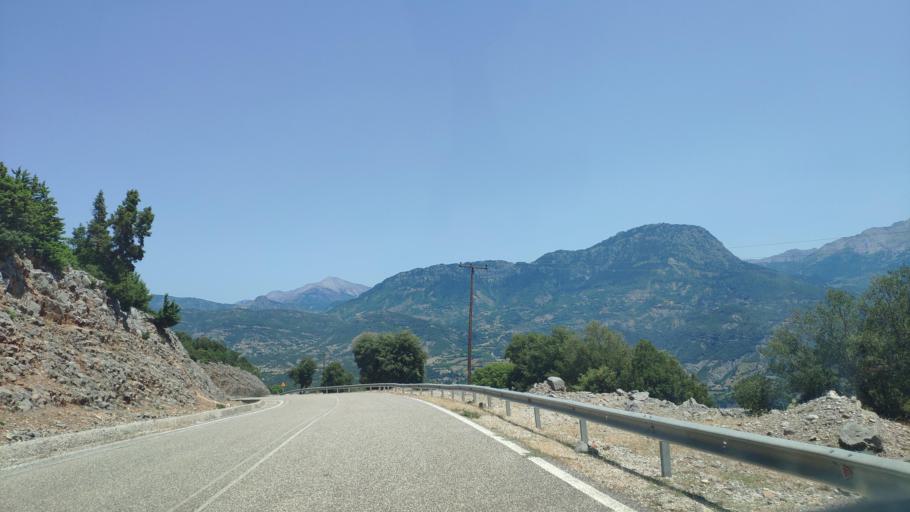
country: GR
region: Central Greece
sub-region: Nomos Evrytanias
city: Kerasochori
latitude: 39.0916
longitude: 21.4112
